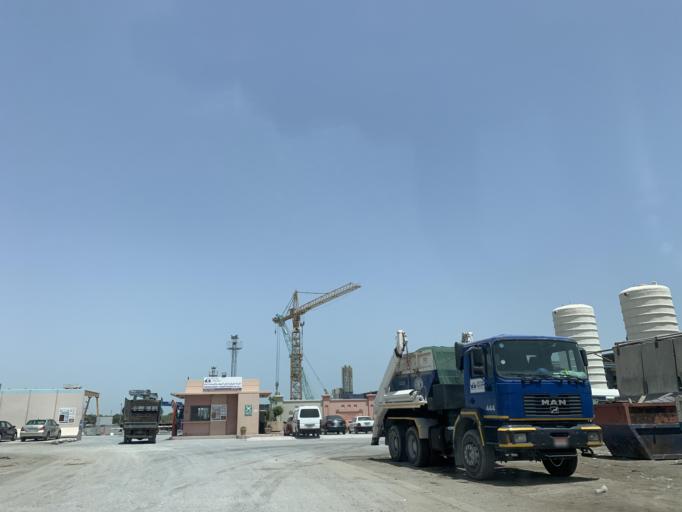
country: BH
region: Northern
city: Sitrah
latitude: 26.1478
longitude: 50.5961
